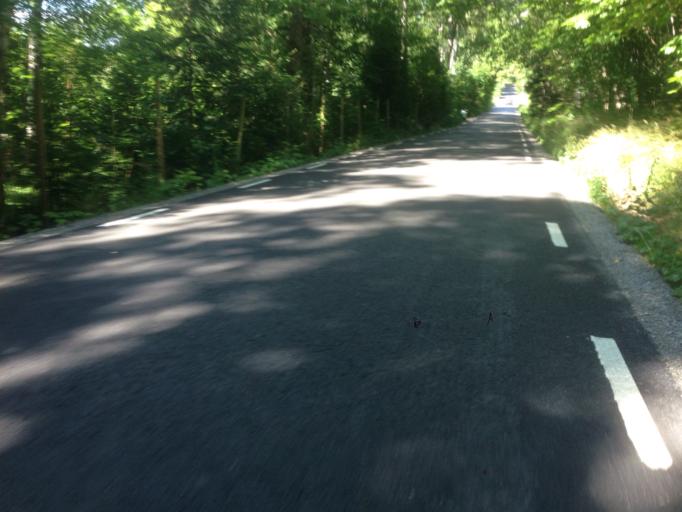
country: SE
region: Stockholm
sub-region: Vaxholms Kommun
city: Vaxholm
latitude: 59.3807
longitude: 18.3750
